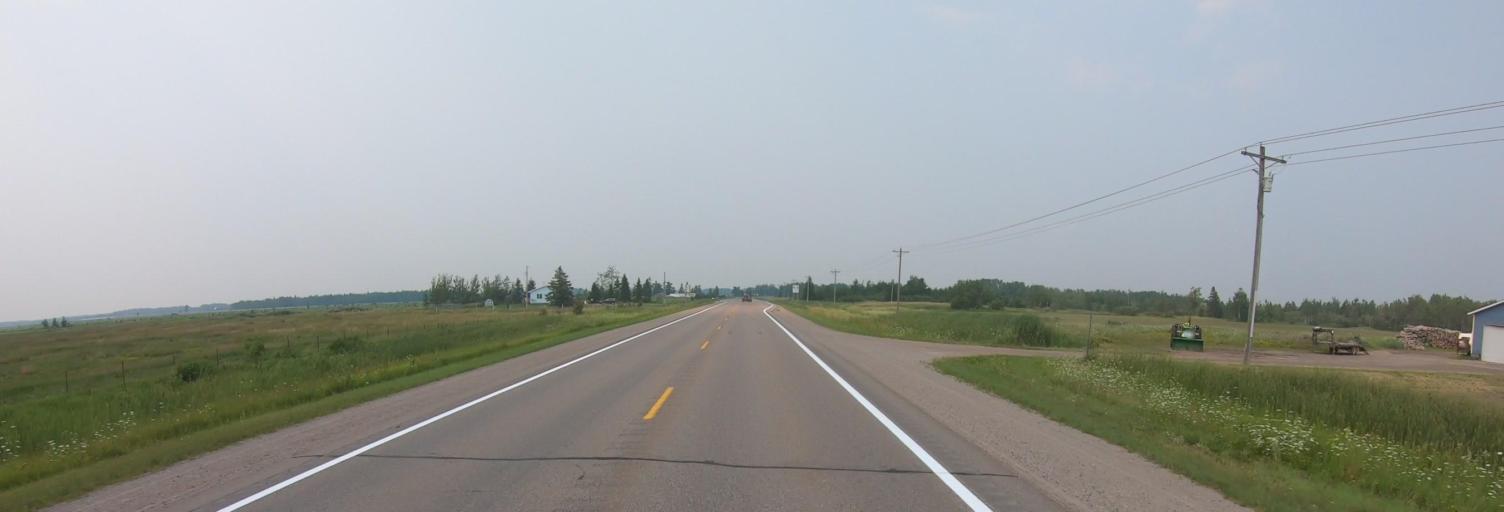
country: US
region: Michigan
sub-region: Chippewa County
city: Sault Ste. Marie
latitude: 46.3590
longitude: -84.3640
